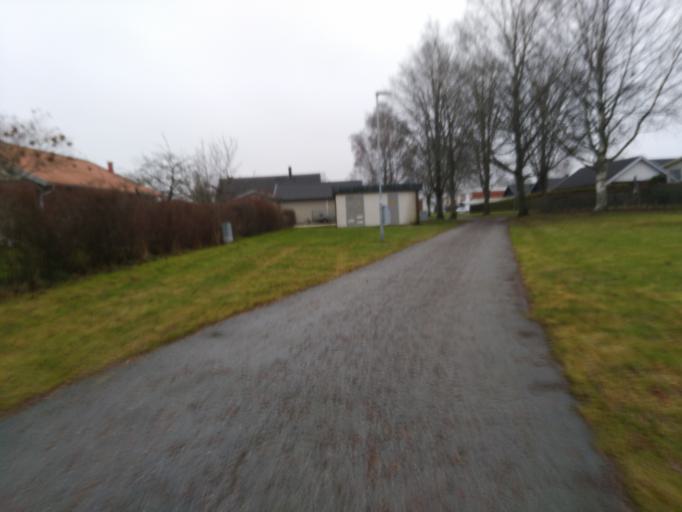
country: SE
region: Vaestra Goetaland
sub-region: Lidkopings Kommun
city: Lidkoping
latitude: 58.4889
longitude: 13.1479
